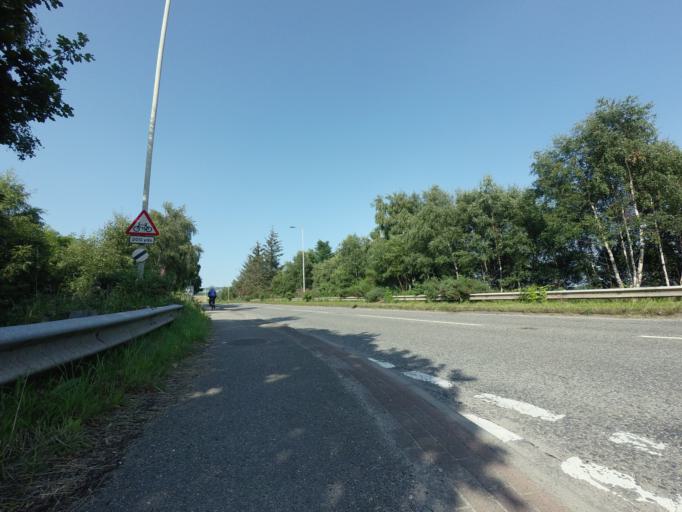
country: GB
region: Scotland
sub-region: Highland
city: Alness
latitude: 57.6820
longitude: -4.2965
